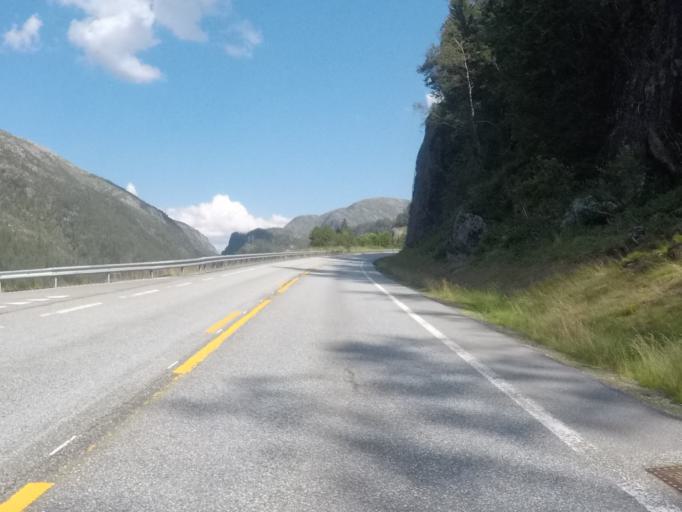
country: NO
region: Hordaland
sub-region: Modalen
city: Mo
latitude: 60.7745
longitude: 5.6229
